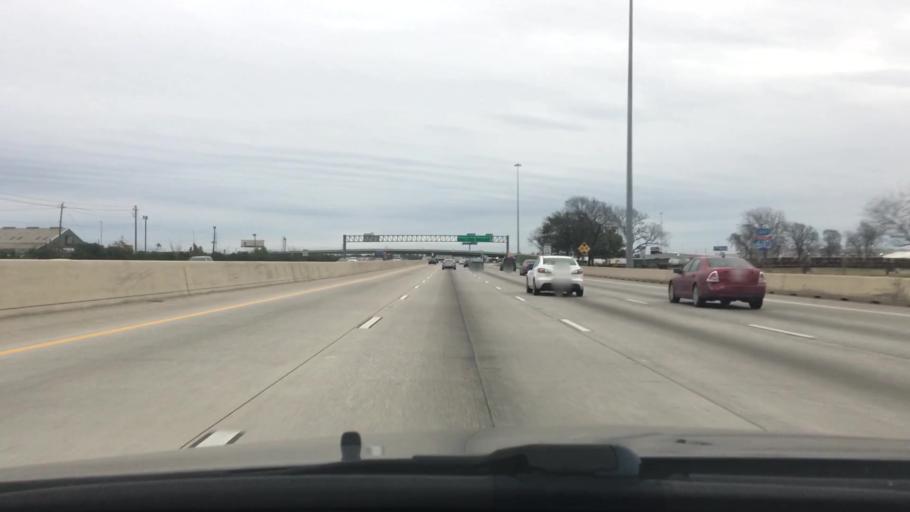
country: US
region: Texas
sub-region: Harris County
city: Houston
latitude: 29.8094
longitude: -95.3122
